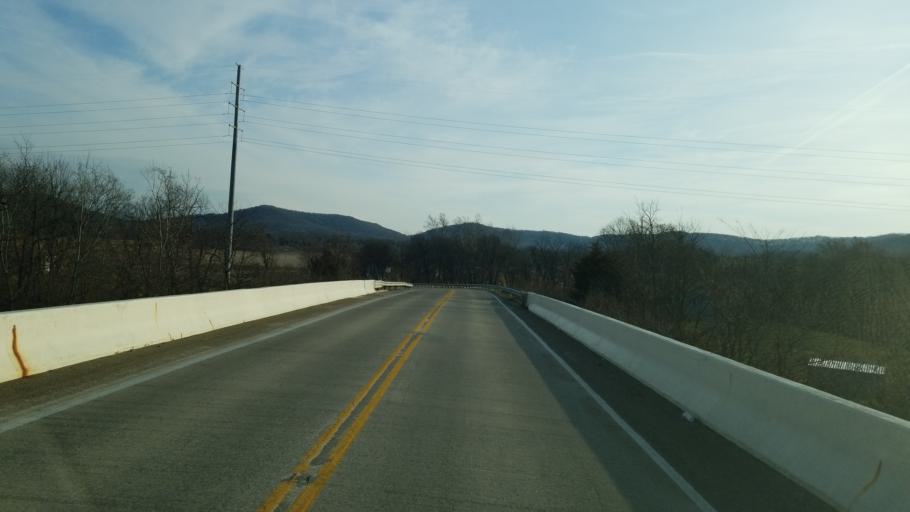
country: US
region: Ohio
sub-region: Ross County
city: Chillicothe
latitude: 39.3849
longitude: -82.9655
